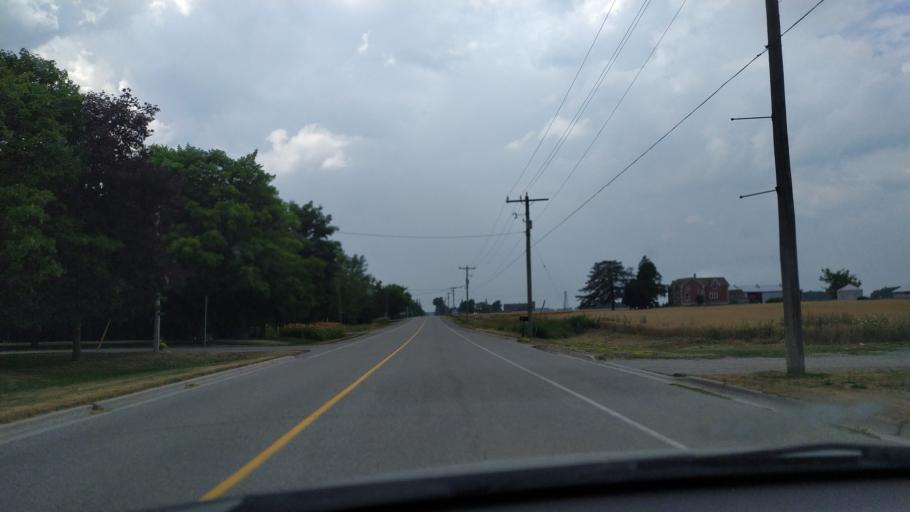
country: CA
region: Ontario
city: Dorchester
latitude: 43.1939
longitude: -81.1493
